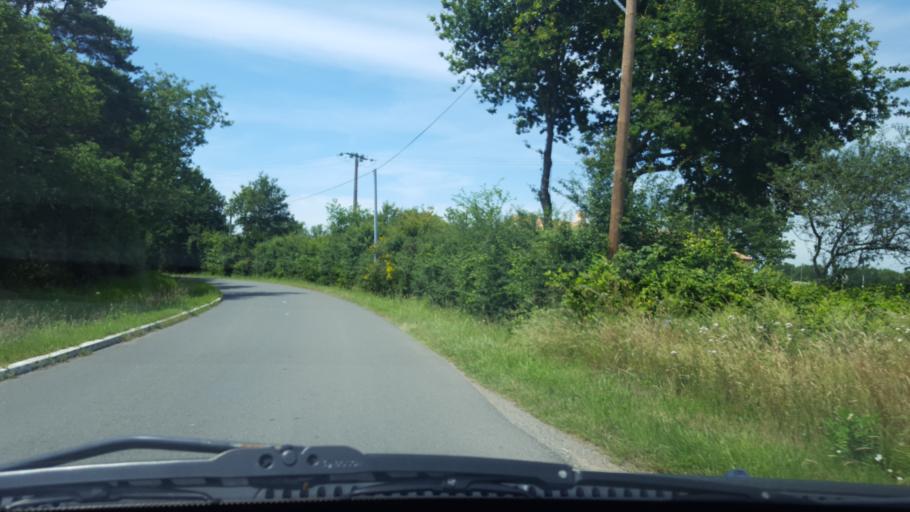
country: FR
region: Pays de la Loire
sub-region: Departement de la Loire-Atlantique
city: La Limouziniere
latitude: 47.0248
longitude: -1.5907
